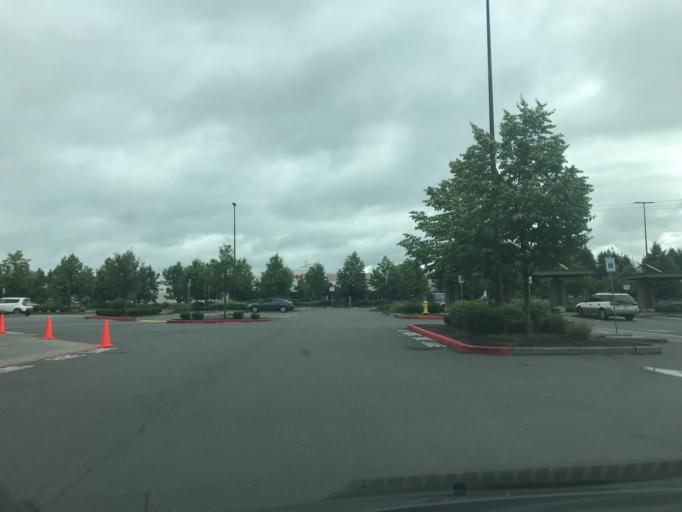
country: US
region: Washington
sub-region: King County
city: Covington
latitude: 47.3548
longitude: -122.1212
